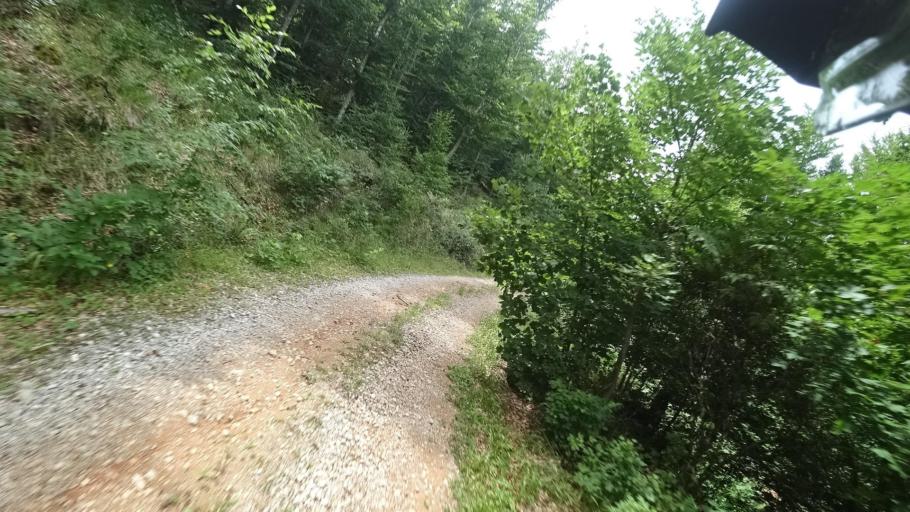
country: BA
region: Federation of Bosnia and Herzegovina
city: Bihac
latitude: 44.6392
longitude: 15.7711
